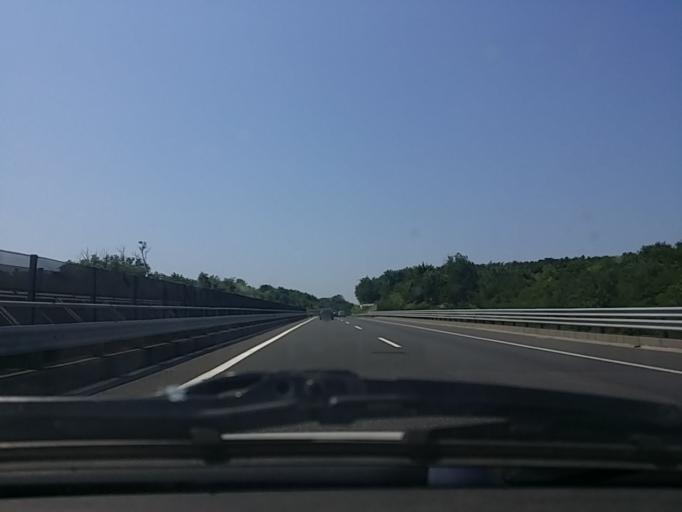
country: HU
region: Somogy
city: Balatonszarszo
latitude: 46.7949
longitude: 17.8001
